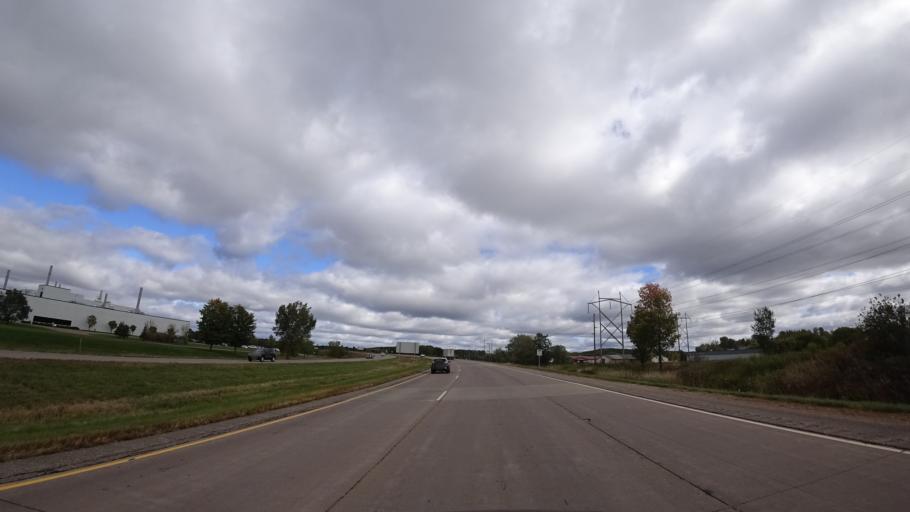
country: US
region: Wisconsin
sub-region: Eau Claire County
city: Eau Claire
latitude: 44.8373
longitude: -91.5394
